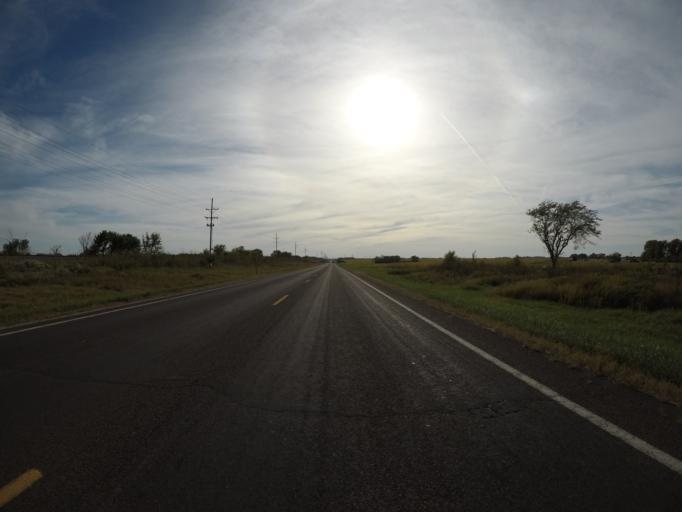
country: US
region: Kansas
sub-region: Johnson County
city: Gardner
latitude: 38.7962
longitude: -94.9615
